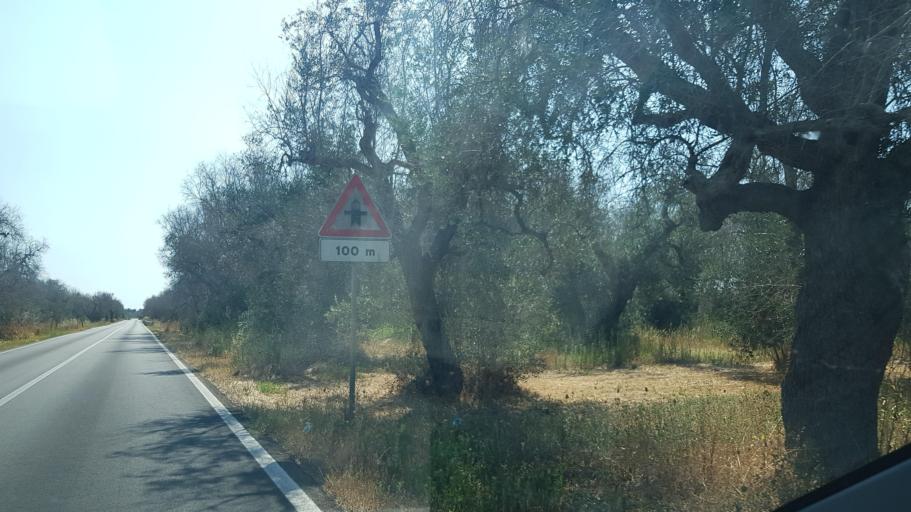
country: IT
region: Apulia
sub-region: Provincia di Lecce
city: Ruffano
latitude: 40.0027
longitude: 18.2846
